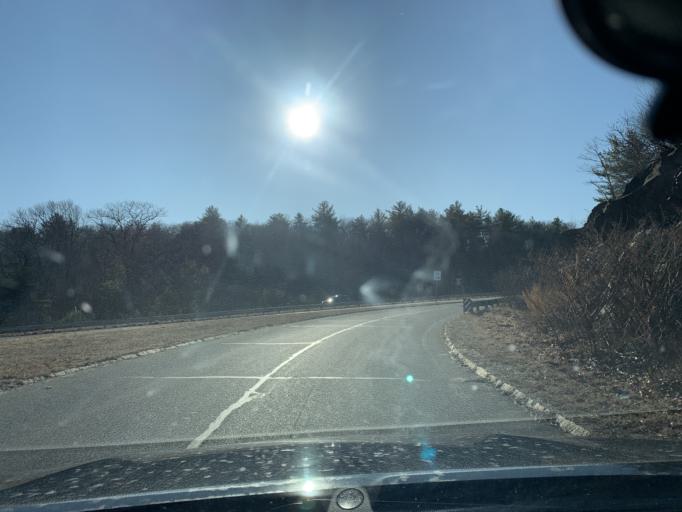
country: US
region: Massachusetts
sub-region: Essex County
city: Essex
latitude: 42.5910
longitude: -70.7918
